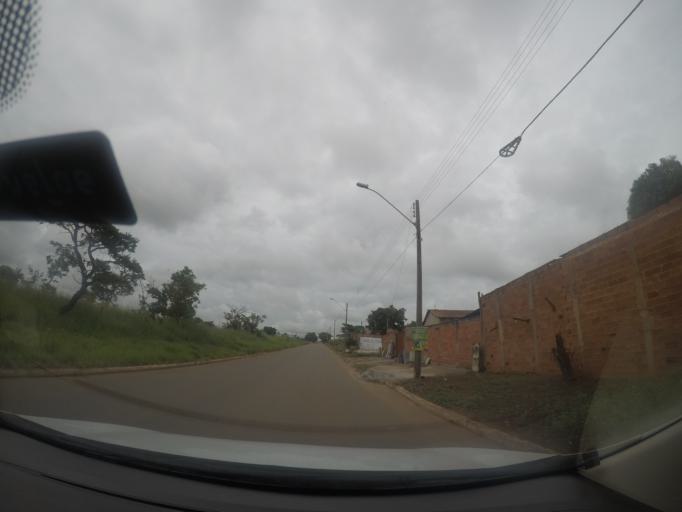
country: BR
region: Goias
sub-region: Trindade
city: Trindade
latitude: -16.6837
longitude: -49.4032
